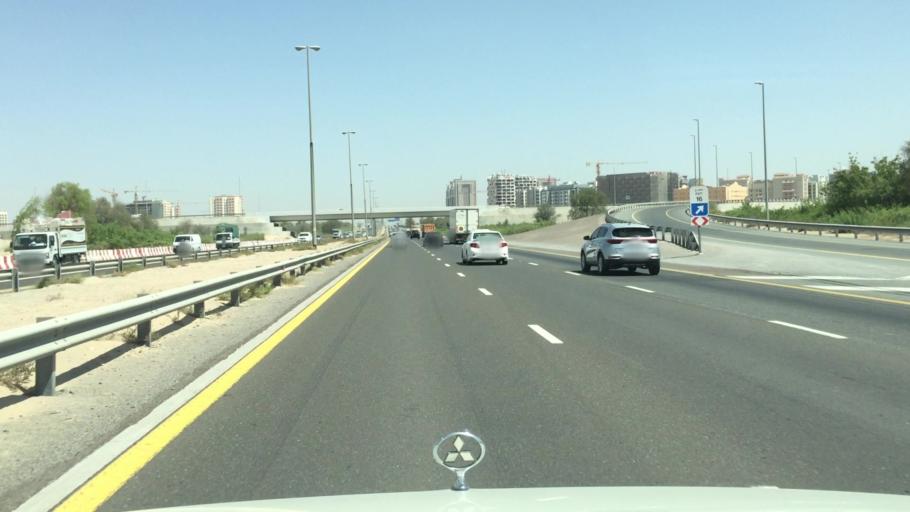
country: AE
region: Dubai
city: Dubai
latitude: 25.1001
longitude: 55.3818
